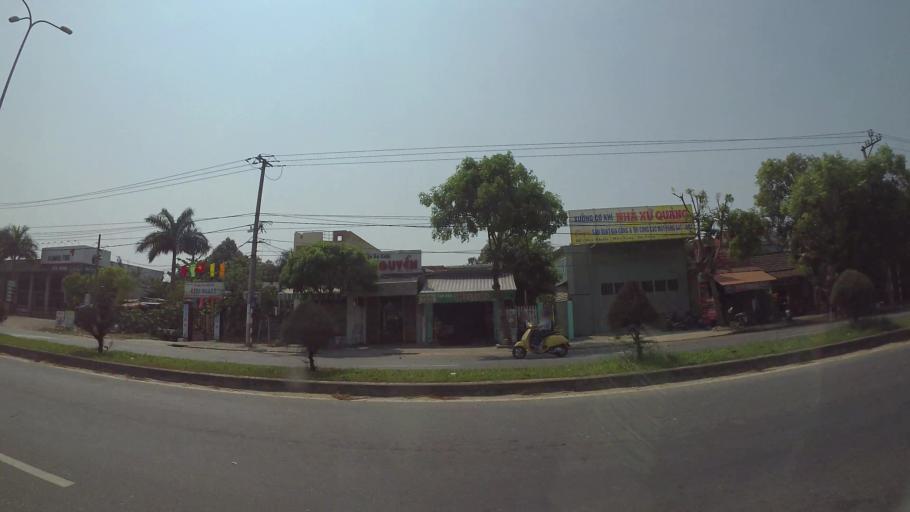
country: VN
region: Da Nang
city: Cam Le
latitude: 15.9753
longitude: 108.2085
